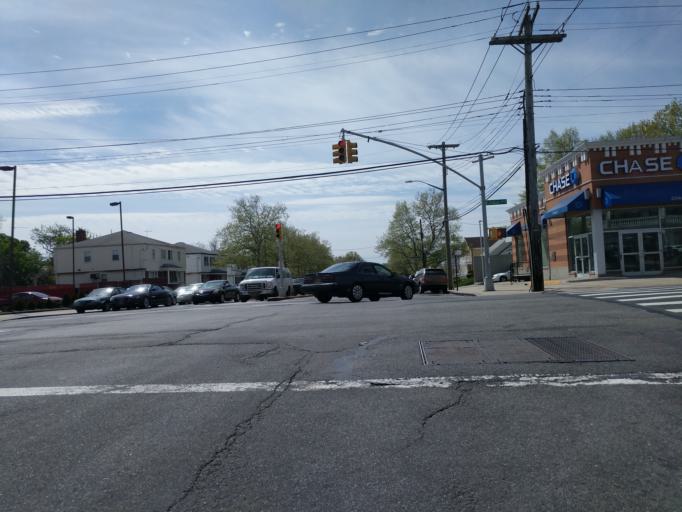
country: US
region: New York
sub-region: Nassau County
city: Bellerose Terrace
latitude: 40.6962
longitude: -73.7463
